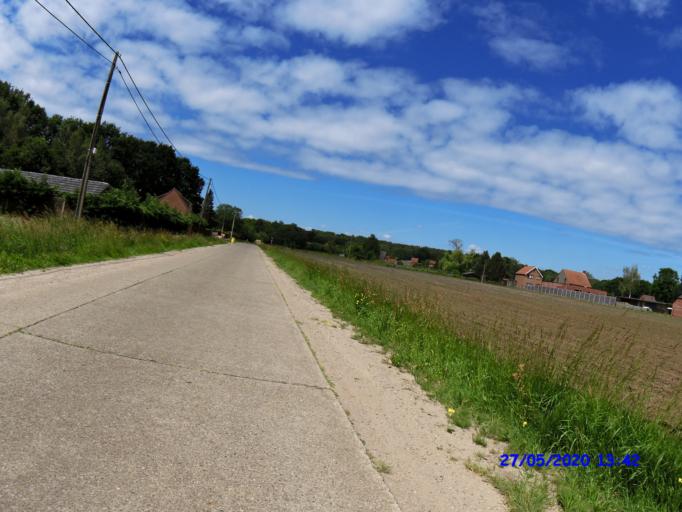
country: BE
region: Flanders
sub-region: Provincie Antwerpen
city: Kasterlee
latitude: 51.2136
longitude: 4.9333
